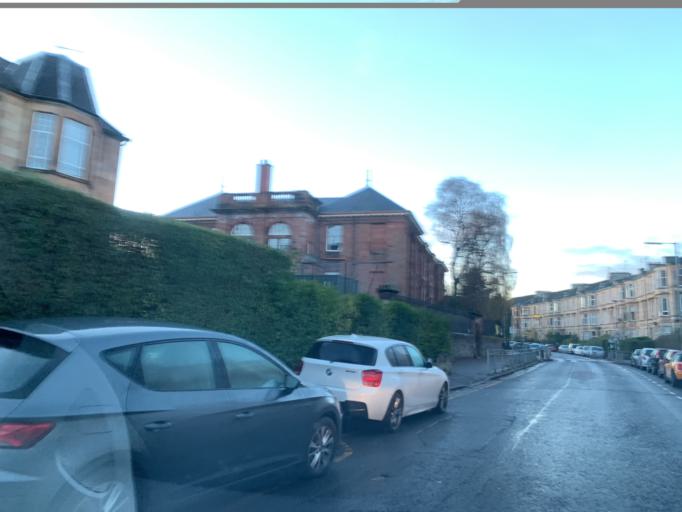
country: GB
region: Scotland
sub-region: East Renfrewshire
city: Giffnock
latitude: 55.8271
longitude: -4.2813
